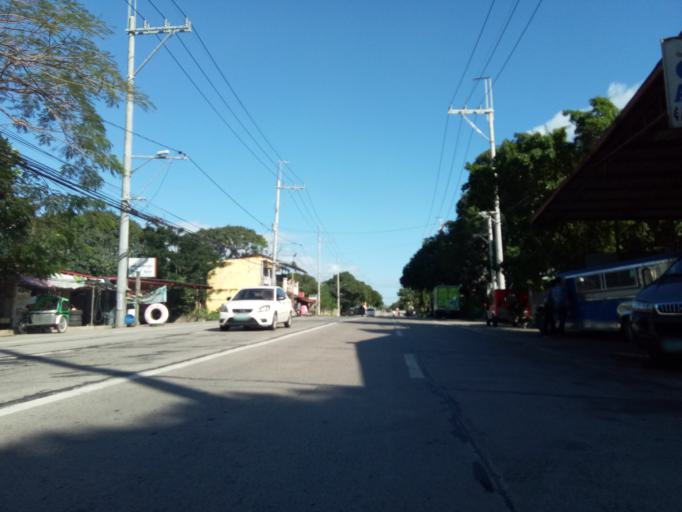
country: PH
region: Calabarzon
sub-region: Province of Cavite
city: Dasmarinas
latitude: 14.3520
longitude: 120.9494
